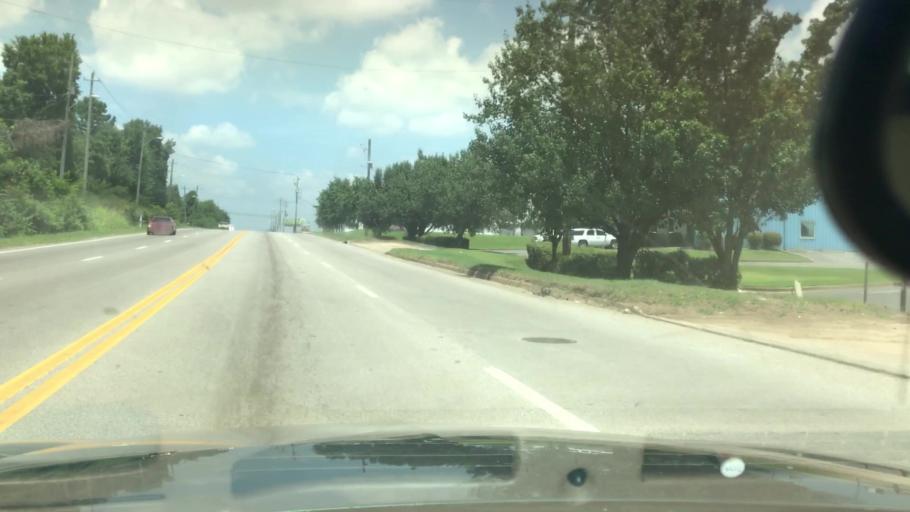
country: US
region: Mississippi
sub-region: De Soto County
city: Southaven
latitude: 35.0162
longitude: -89.9367
